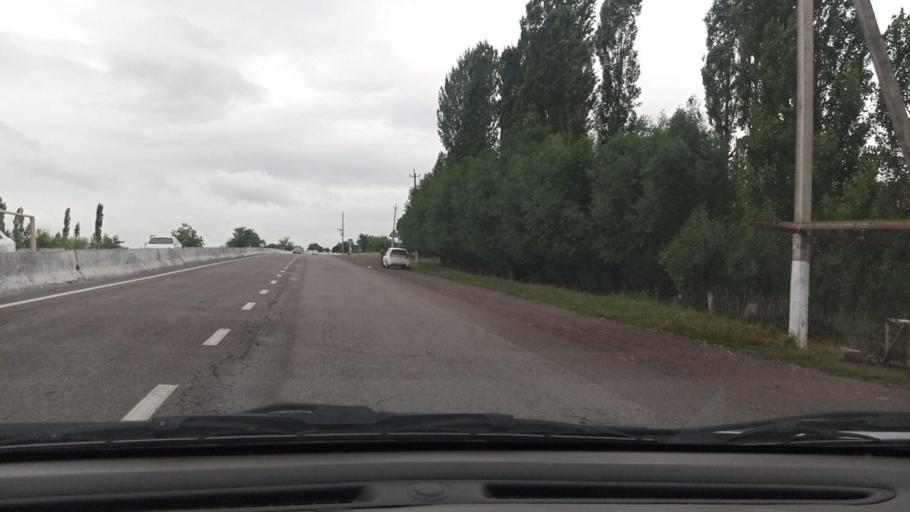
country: UZ
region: Toshkent
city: Angren
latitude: 40.9614
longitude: 69.9452
